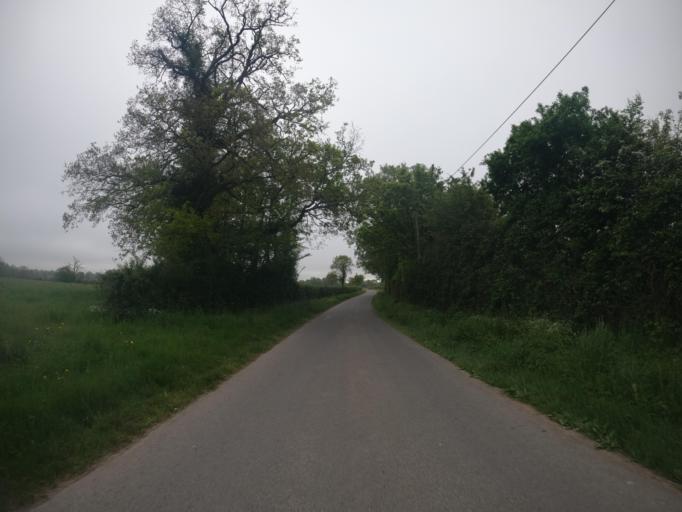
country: FR
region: Poitou-Charentes
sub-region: Departement des Deux-Sevres
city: Chiche
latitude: 46.8573
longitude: -0.3445
